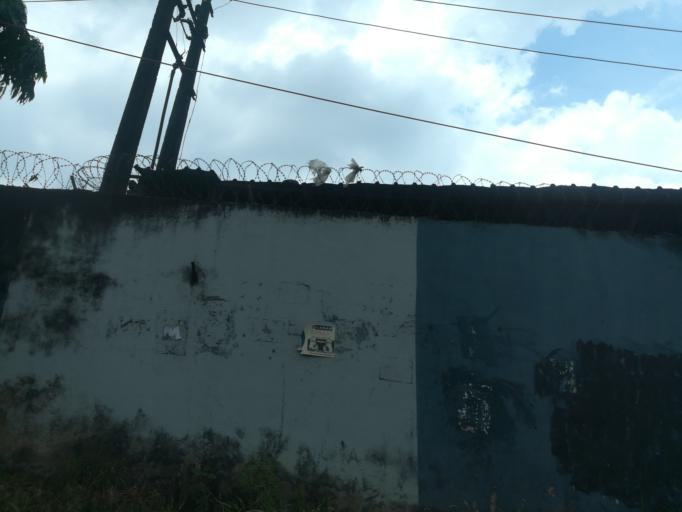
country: NG
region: Lagos
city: Ojota
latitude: 6.5895
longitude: 3.3765
